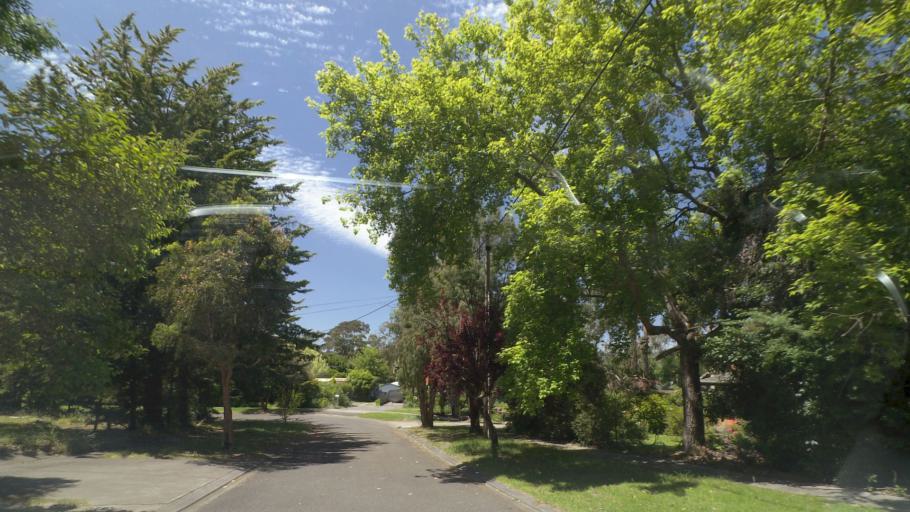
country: AU
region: Victoria
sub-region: Maroondah
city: Croydon North
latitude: -37.7576
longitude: 145.2887
